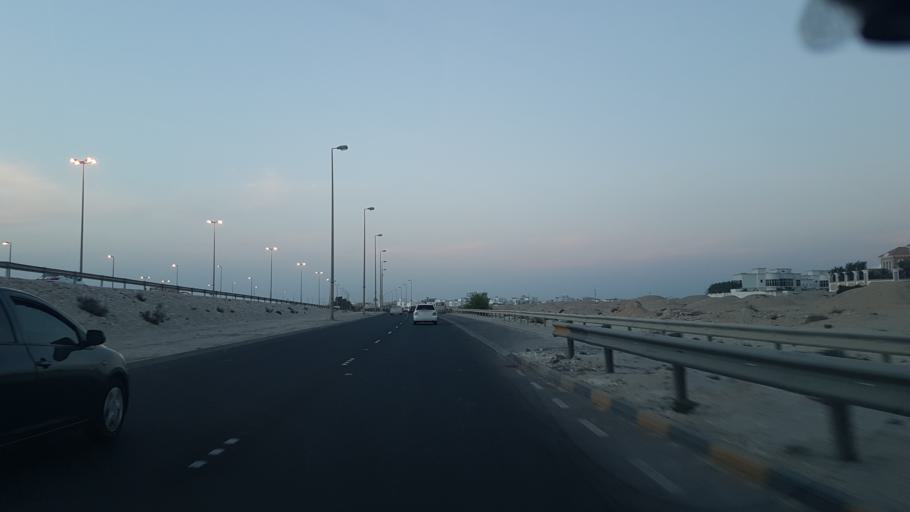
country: BH
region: Central Governorate
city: Madinat Hamad
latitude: 26.1424
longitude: 50.5108
